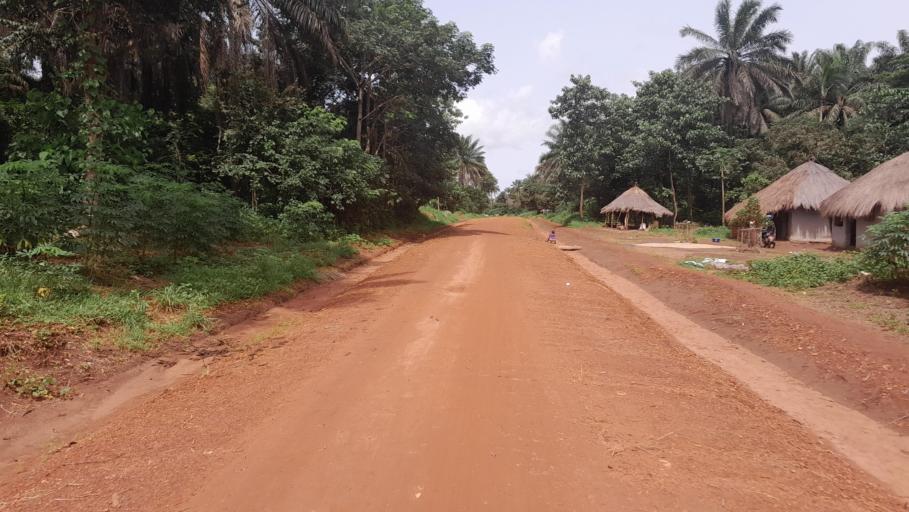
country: GN
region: Boke
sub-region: Boffa
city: Boffa
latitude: 10.0313
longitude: -13.8790
